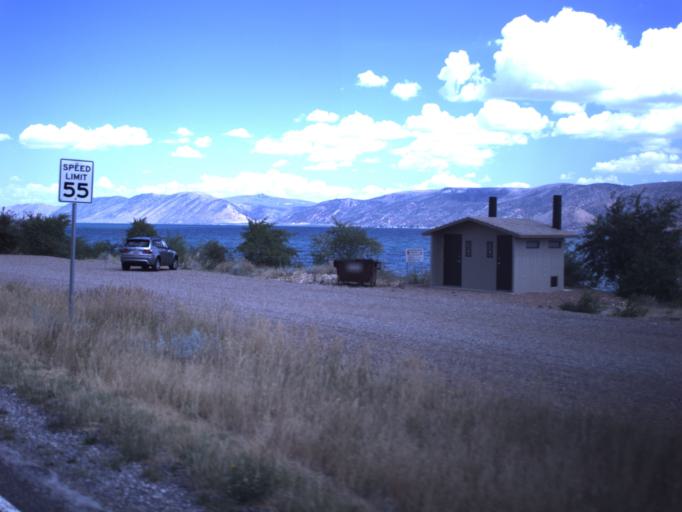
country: US
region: Utah
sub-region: Rich County
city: Randolph
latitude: 41.8628
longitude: -111.3651
